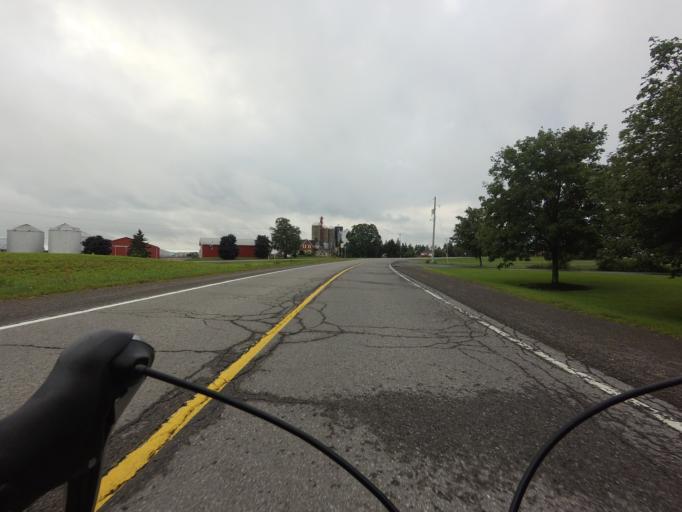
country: CA
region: Ontario
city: Bells Corners
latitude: 45.1399
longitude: -75.7741
